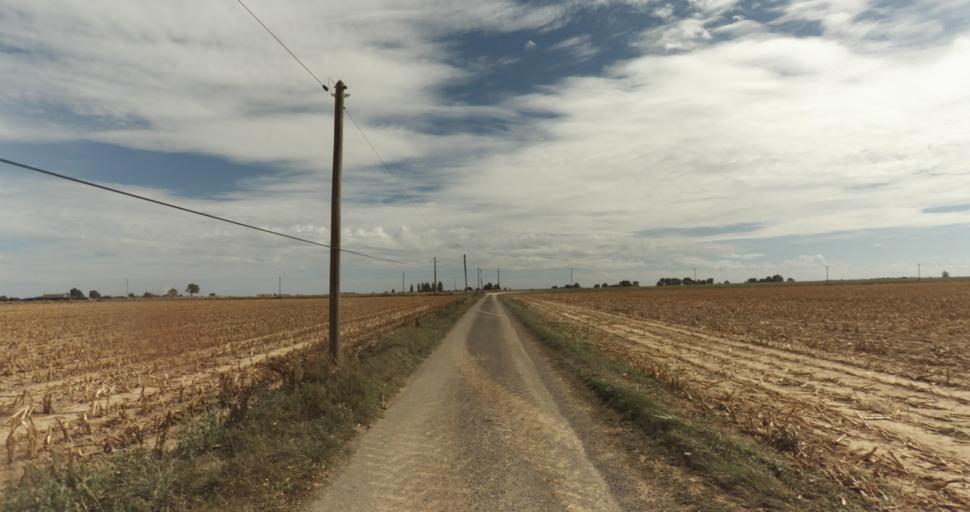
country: FR
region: Lower Normandy
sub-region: Departement du Calvados
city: Orbec
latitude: 48.9536
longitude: 0.3988
